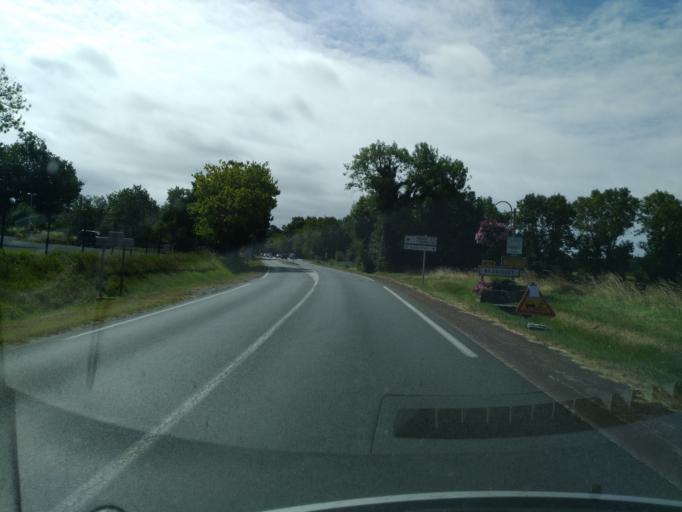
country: FR
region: Poitou-Charentes
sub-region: Departement de la Charente-Maritime
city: Breuillet
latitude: 45.7020
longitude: -1.0571
